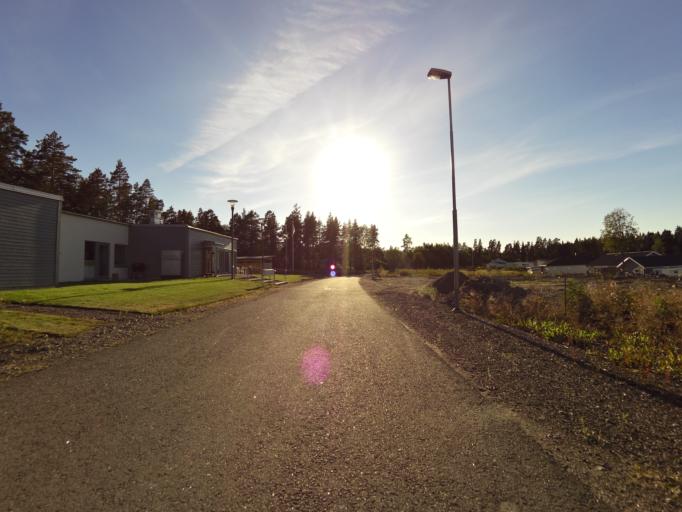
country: SE
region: Gaevleborg
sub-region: Gavle Kommun
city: Gavle
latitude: 60.6433
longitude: 17.1330
